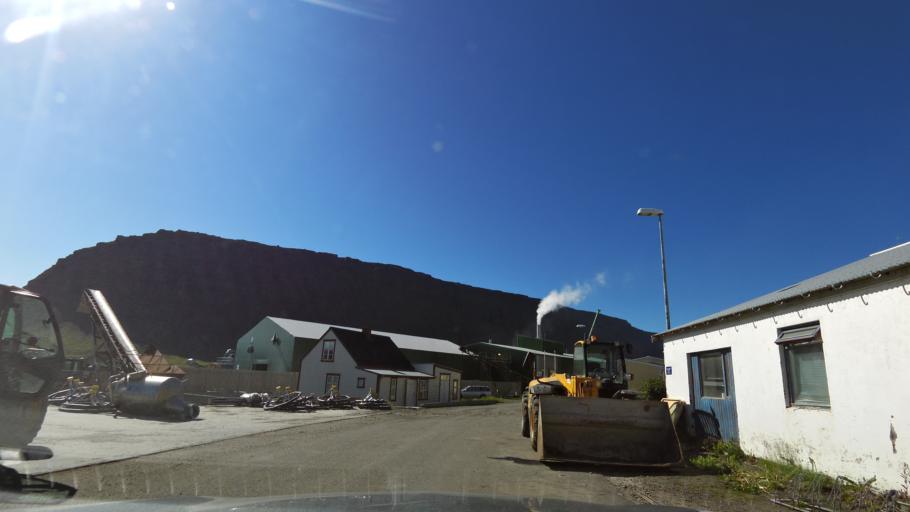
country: IS
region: Westfjords
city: Isafjoerdur
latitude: 65.6866
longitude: -23.5967
